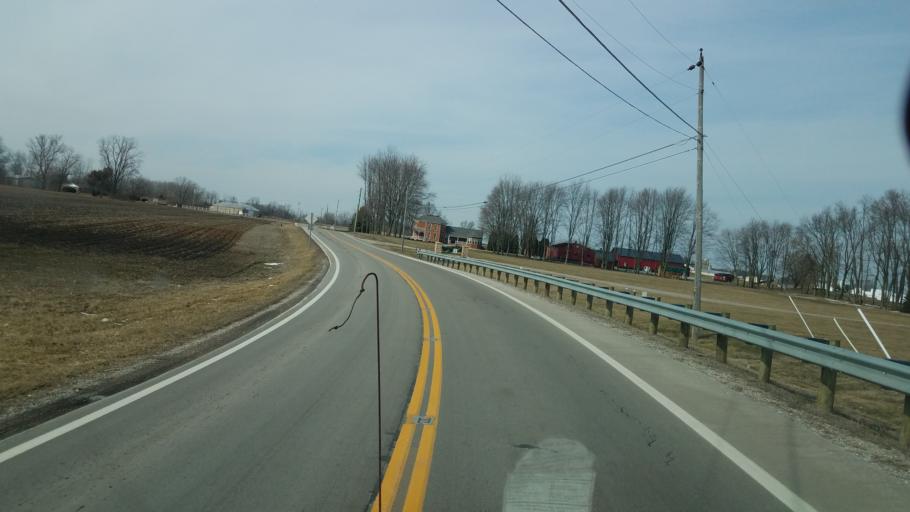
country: US
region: Ohio
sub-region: Delaware County
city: Delaware
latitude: 40.3596
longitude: -83.1441
